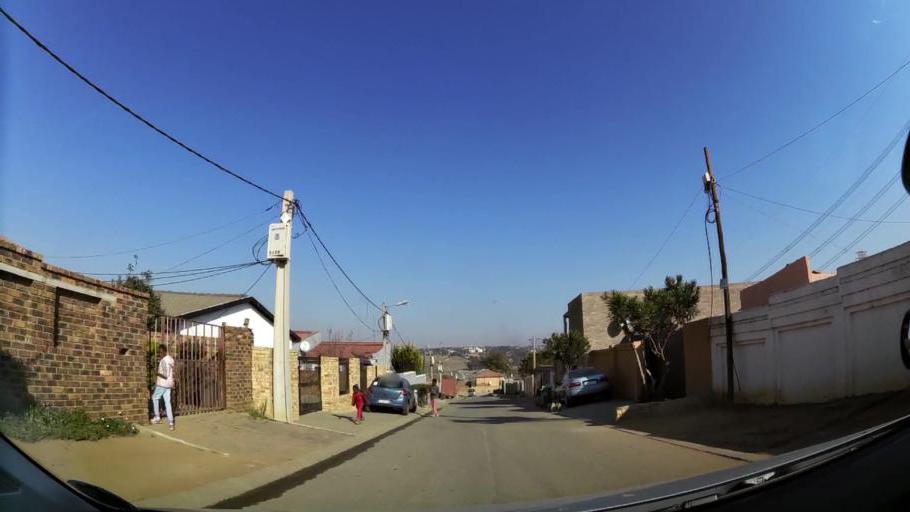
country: ZA
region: Gauteng
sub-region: City of Johannesburg Metropolitan Municipality
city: Modderfontein
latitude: -26.0888
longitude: 28.1141
